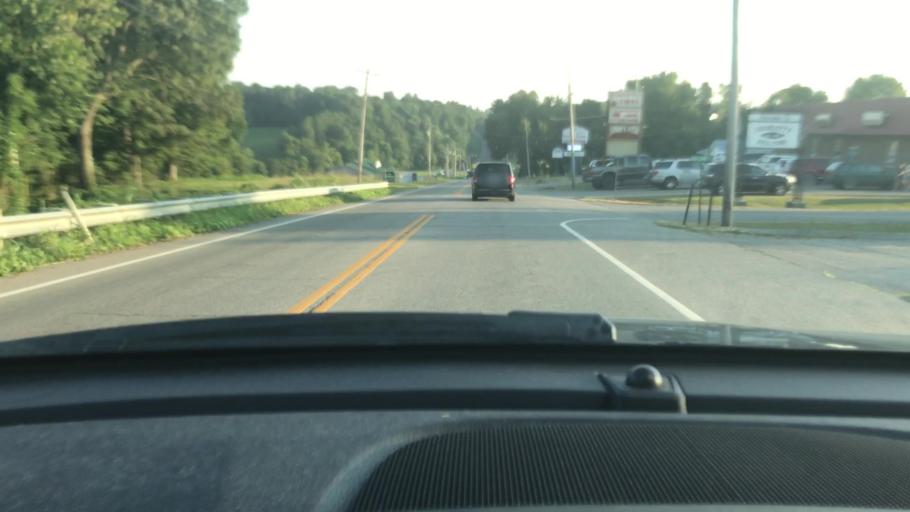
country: US
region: Tennessee
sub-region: Dickson County
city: Charlotte
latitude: 36.1675
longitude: -87.3508
